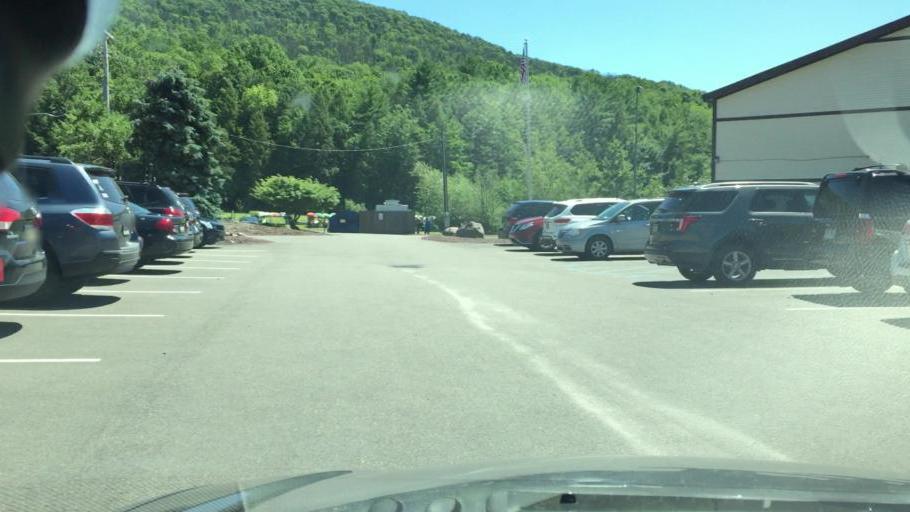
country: US
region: Pennsylvania
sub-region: Luzerne County
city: Freeland
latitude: 41.0498
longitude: -75.9177
